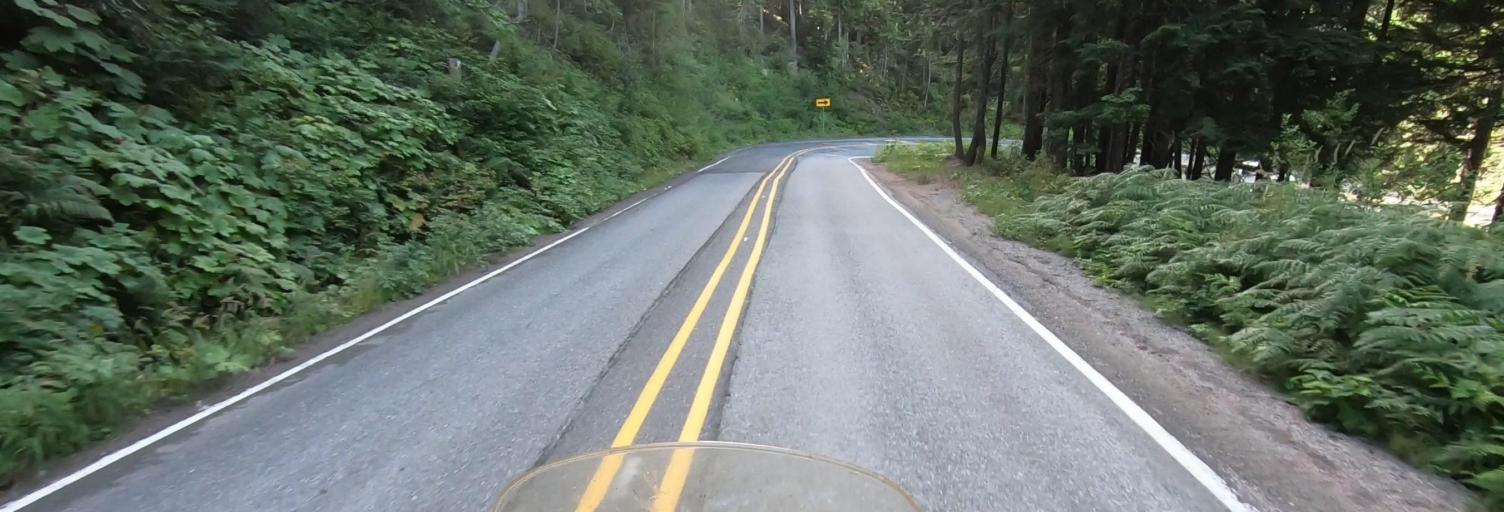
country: CA
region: British Columbia
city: Agassiz
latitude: 48.8753
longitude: -121.6733
